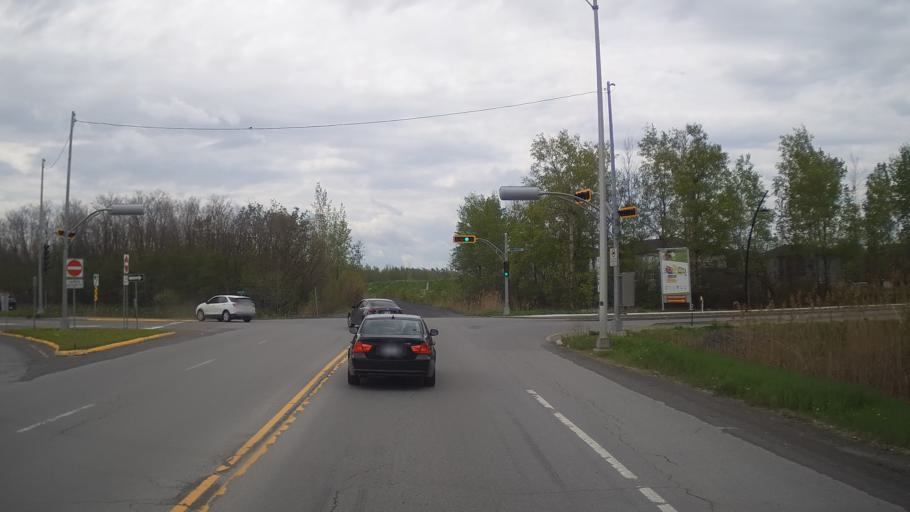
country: CA
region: Quebec
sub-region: Monteregie
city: La Prairie
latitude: 45.4028
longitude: -73.4645
